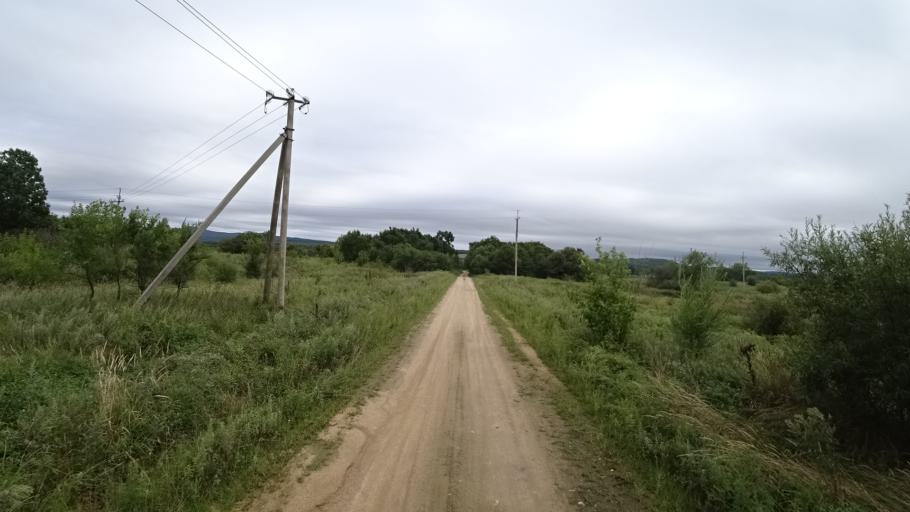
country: RU
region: Primorskiy
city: Rettikhovka
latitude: 44.1326
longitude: 132.6341
